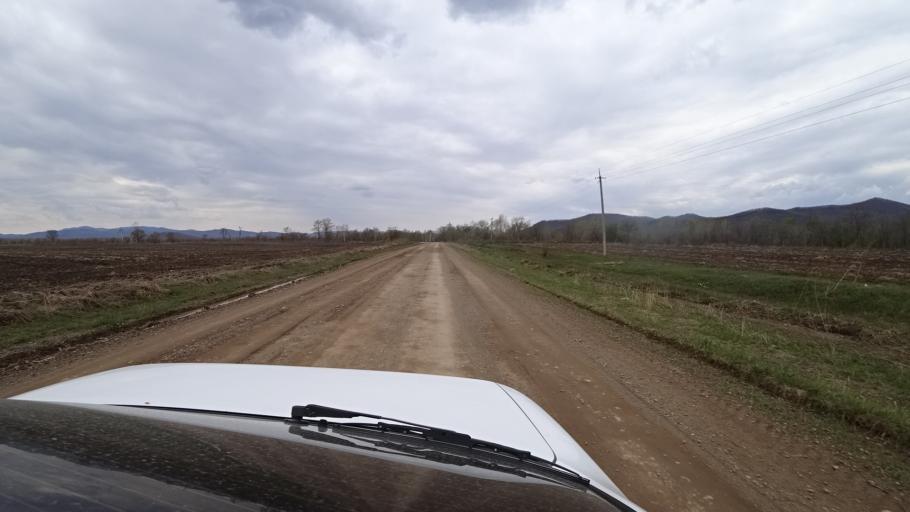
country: RU
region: Primorskiy
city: Novopokrovka
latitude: 45.5576
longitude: 134.3531
